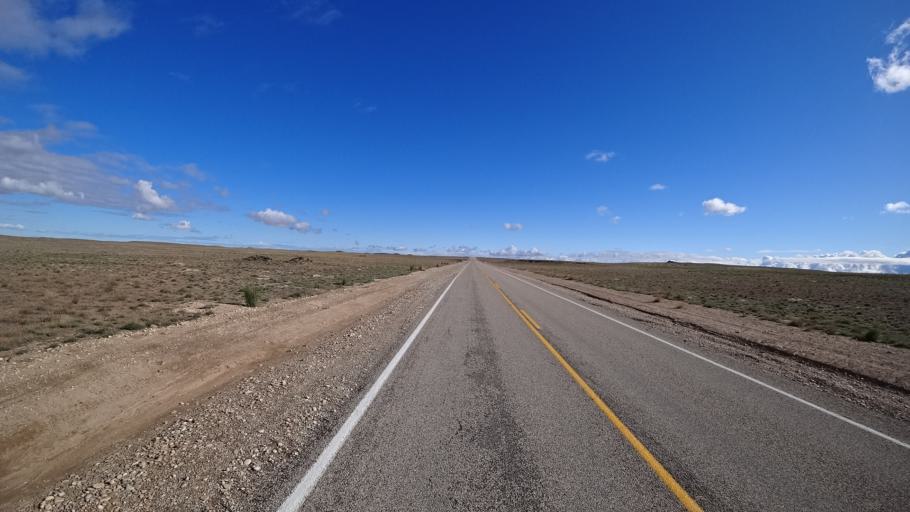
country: US
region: Idaho
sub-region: Ada County
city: Kuna
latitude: 43.3469
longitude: -116.4139
